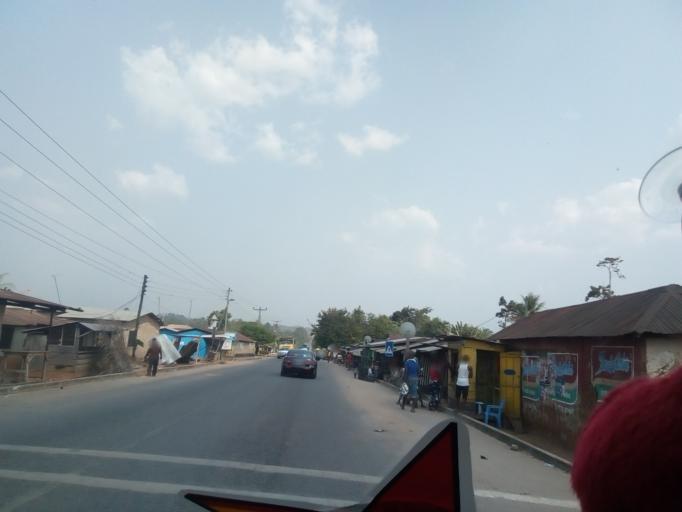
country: GH
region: Eastern
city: Suhum
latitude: 6.0426
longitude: -0.4347
